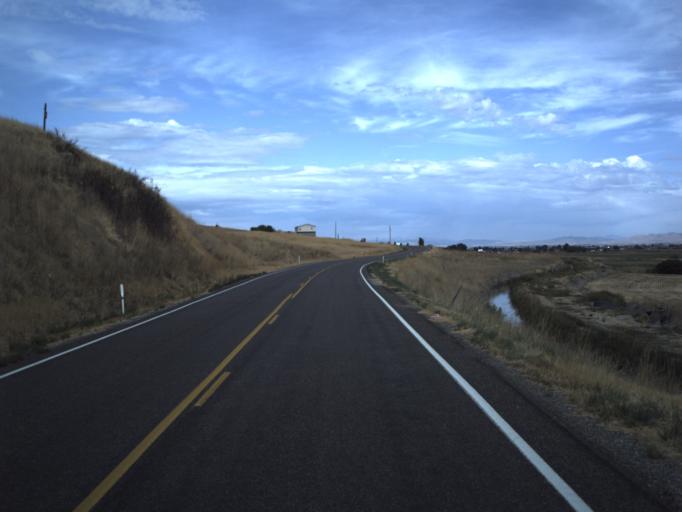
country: US
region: Utah
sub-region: Cache County
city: Benson
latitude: 41.8900
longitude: -111.9498
